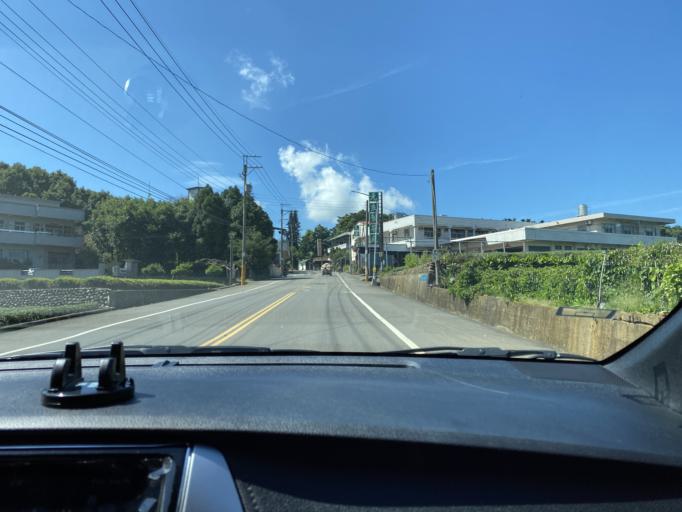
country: TW
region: Taiwan
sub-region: Nantou
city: Nantou
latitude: 23.8458
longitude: 120.6299
